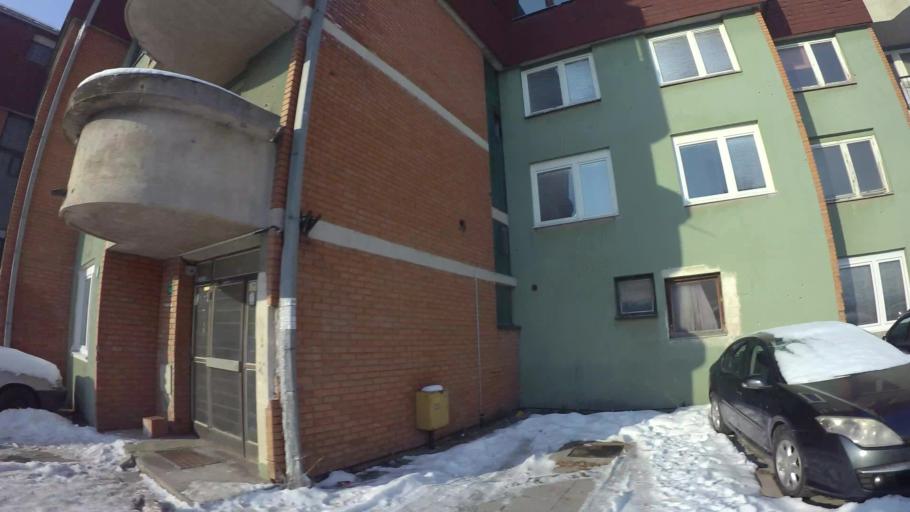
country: BA
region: Federation of Bosnia and Herzegovina
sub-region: Kanton Sarajevo
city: Sarajevo
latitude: 43.8222
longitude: 18.3545
